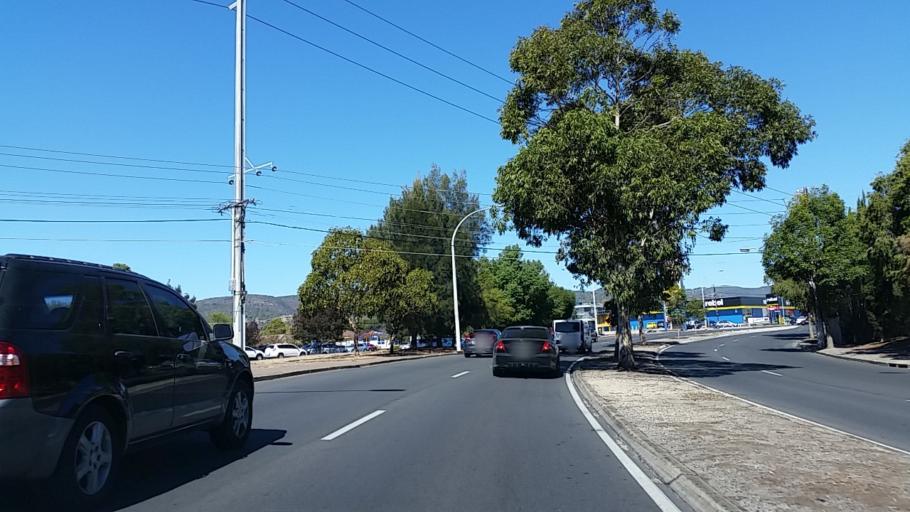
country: AU
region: South Australia
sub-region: Campbelltown
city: Paradise
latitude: -34.8776
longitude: 138.6730
